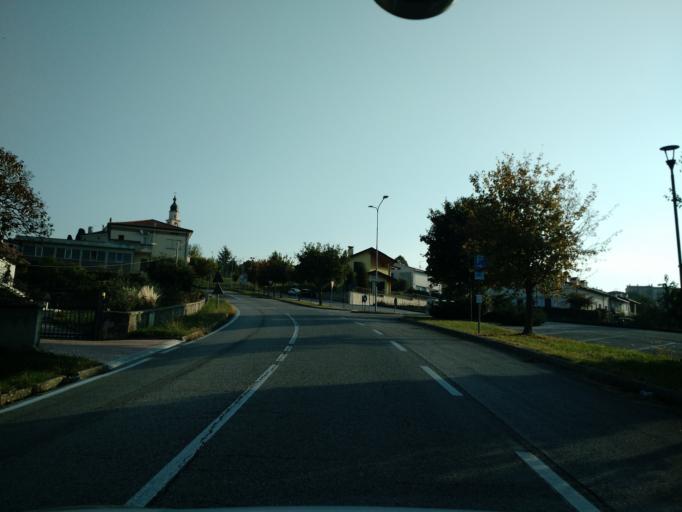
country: IT
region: Veneto
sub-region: Provincia di Vicenza
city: Salcedo
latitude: 45.7569
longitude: 11.5627
